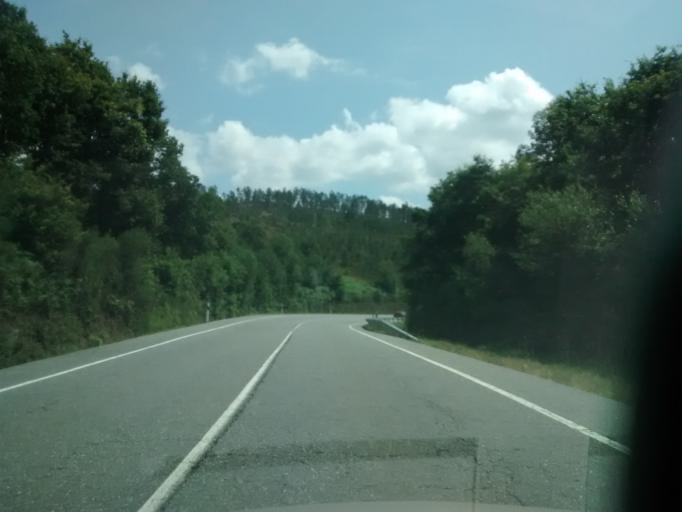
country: ES
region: Galicia
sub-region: Provincia de Pontevedra
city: Forcarei
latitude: 42.5429
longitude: -8.3435
